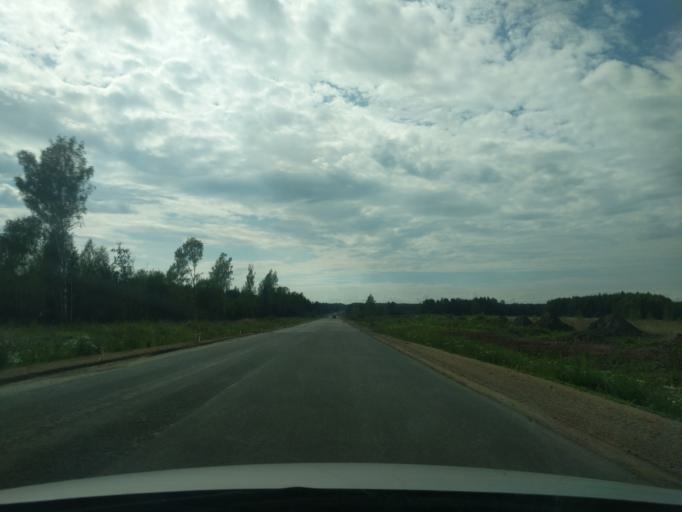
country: RU
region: Kostroma
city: Sudislavl'
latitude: 57.8585
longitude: 41.6111
